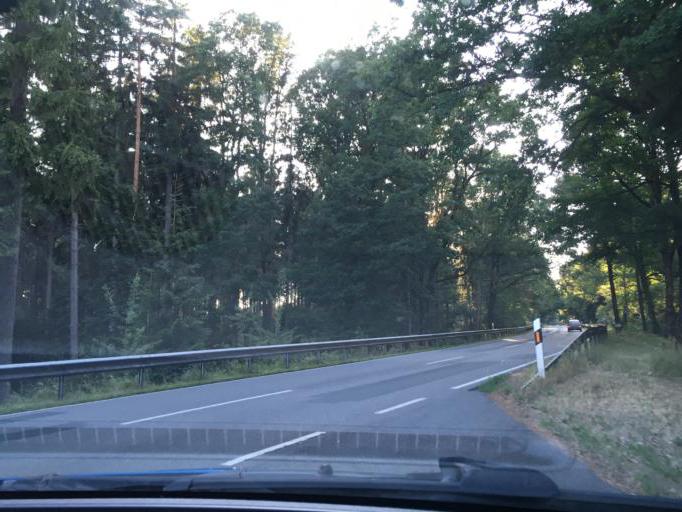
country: DE
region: Lower Saxony
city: Unterluss
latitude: 52.8022
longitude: 10.3768
